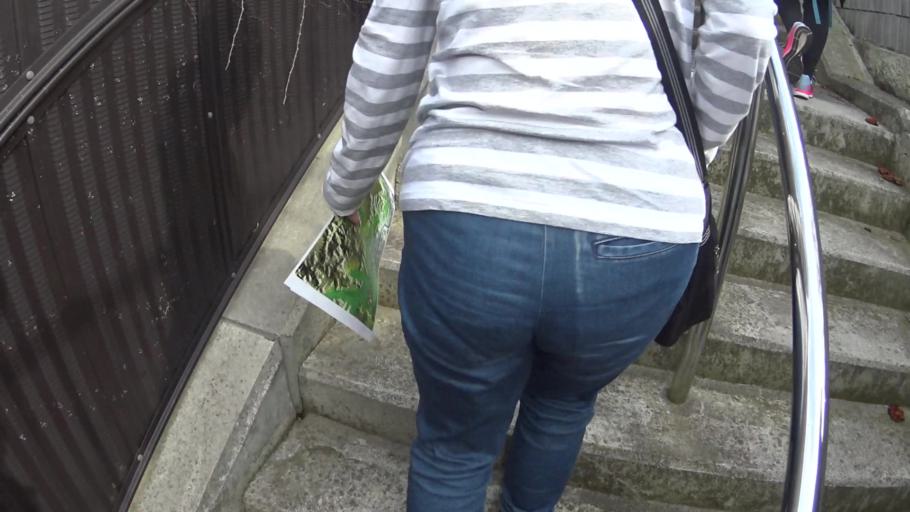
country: JP
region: Kanagawa
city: Kamakura
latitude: 35.3222
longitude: 139.5133
